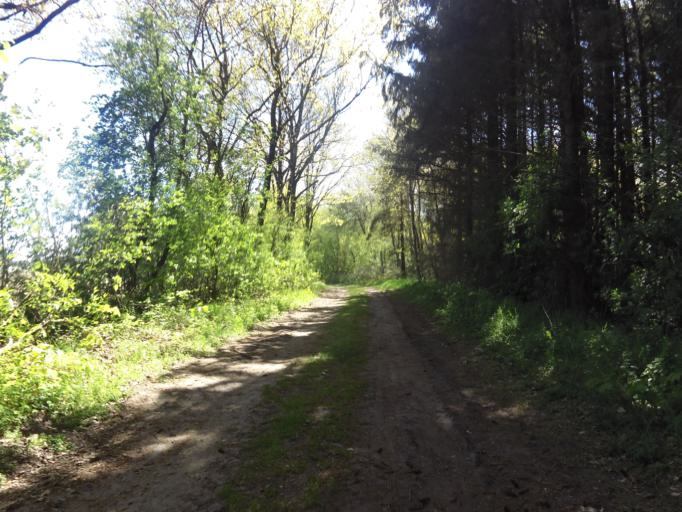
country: DK
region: South Denmark
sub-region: Tonder Kommune
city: Sherrebek
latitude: 55.2350
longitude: 8.7316
